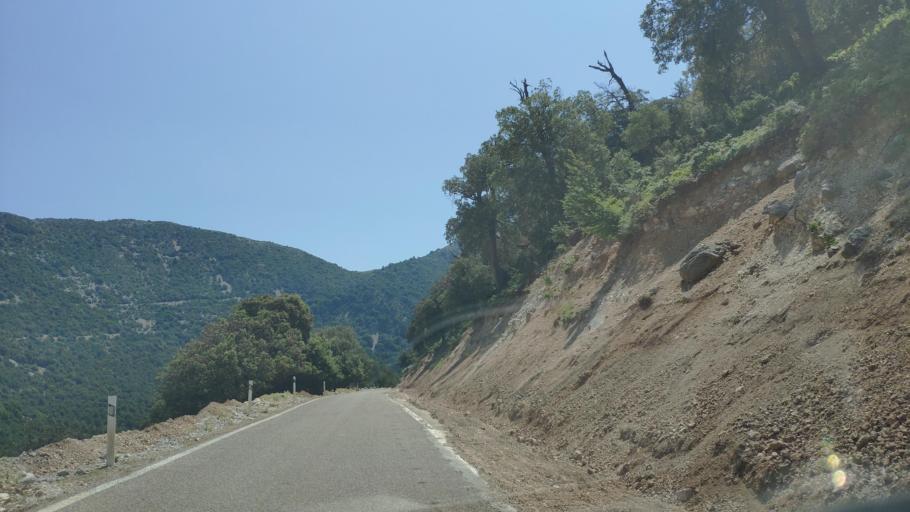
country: GR
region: West Greece
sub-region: Nomos Aitolias kai Akarnanias
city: Krikellos
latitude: 39.0186
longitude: 21.3456
